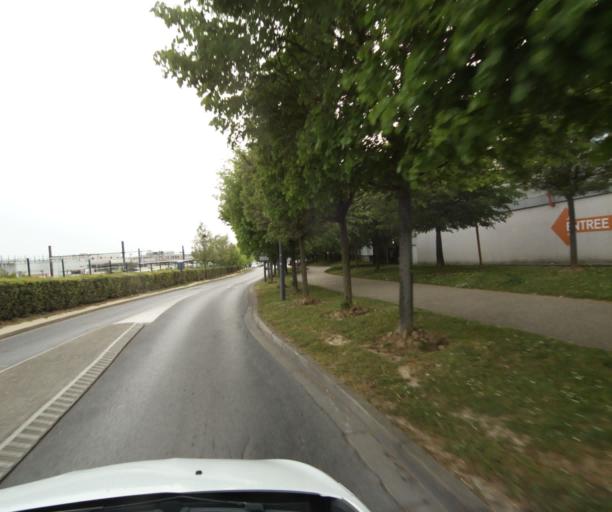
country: FR
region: Ile-de-France
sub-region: Departement de Seine-et-Marne
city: Torcy
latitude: 48.8401
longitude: 2.6562
